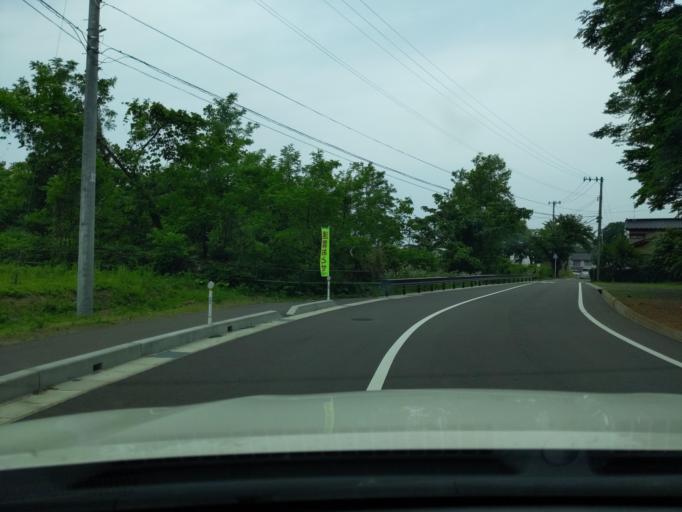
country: JP
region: Niigata
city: Kashiwazaki
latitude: 37.3601
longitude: 138.5394
